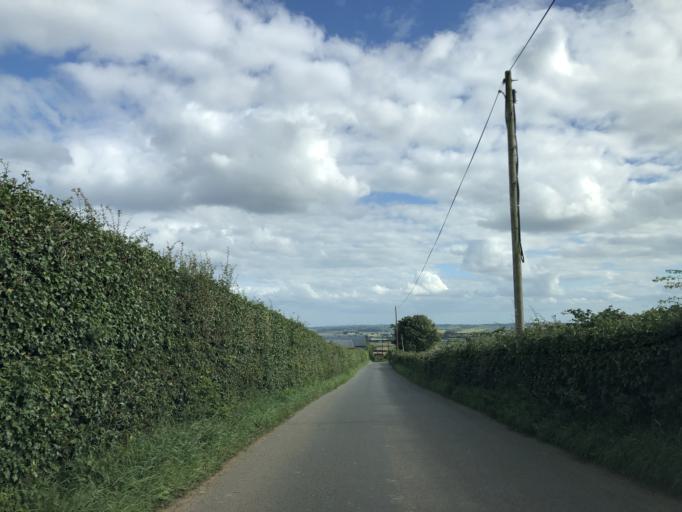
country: GB
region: Northern Ireland
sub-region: Ards District
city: Newtownards
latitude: 54.5742
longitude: -5.7162
